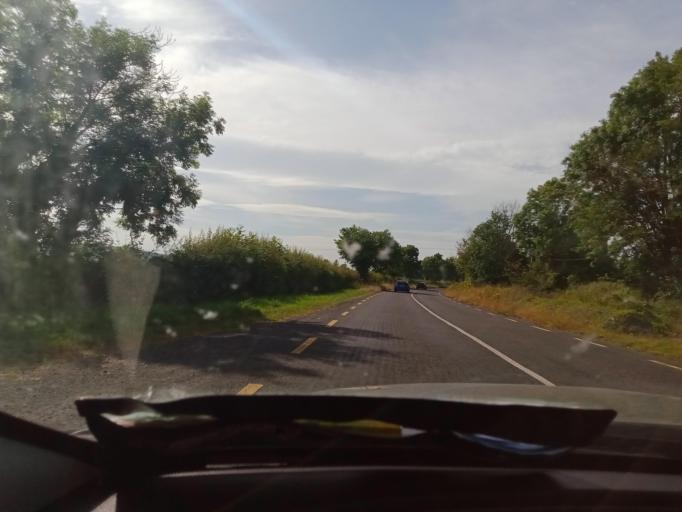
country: IE
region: Leinster
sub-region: Laois
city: Mountmellick
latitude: 53.1219
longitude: -7.3703
